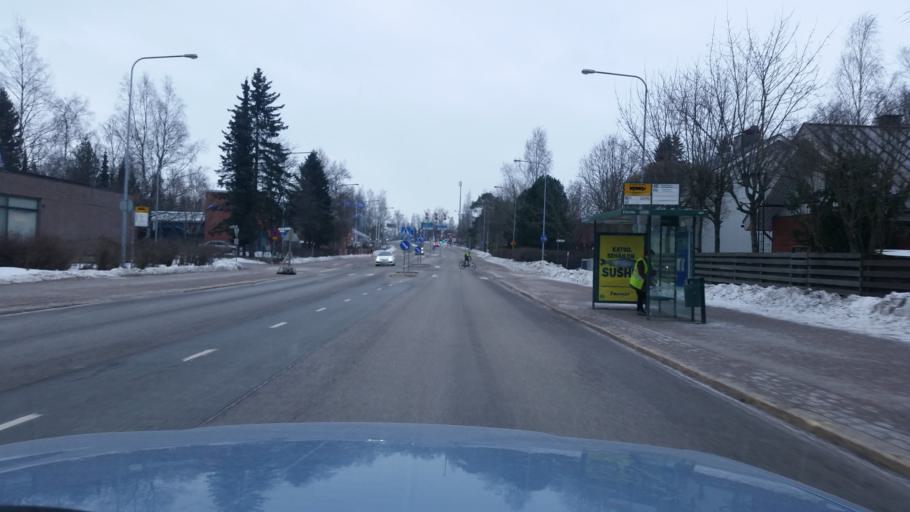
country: FI
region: Uusimaa
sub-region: Helsinki
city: Helsinki
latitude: 60.2445
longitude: 24.9251
